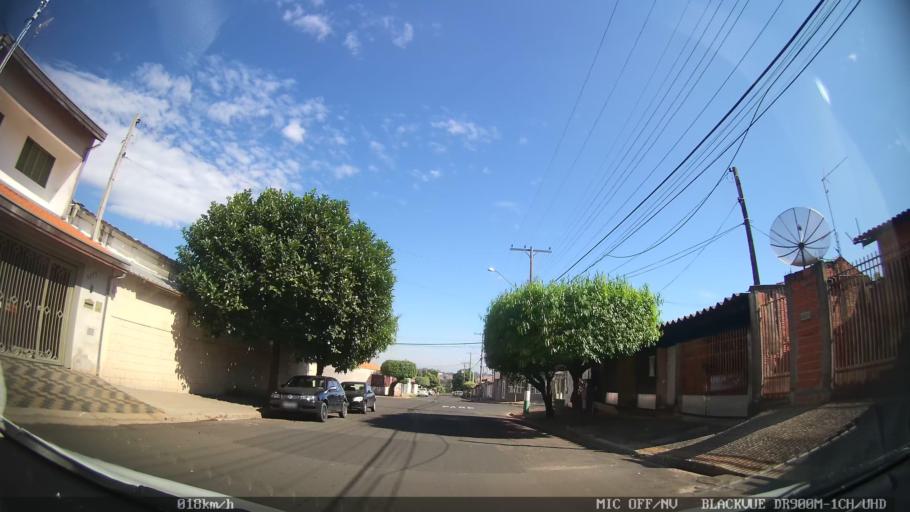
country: BR
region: Sao Paulo
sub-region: Santa Barbara D'Oeste
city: Santa Barbara d'Oeste
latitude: -22.7424
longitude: -47.3820
